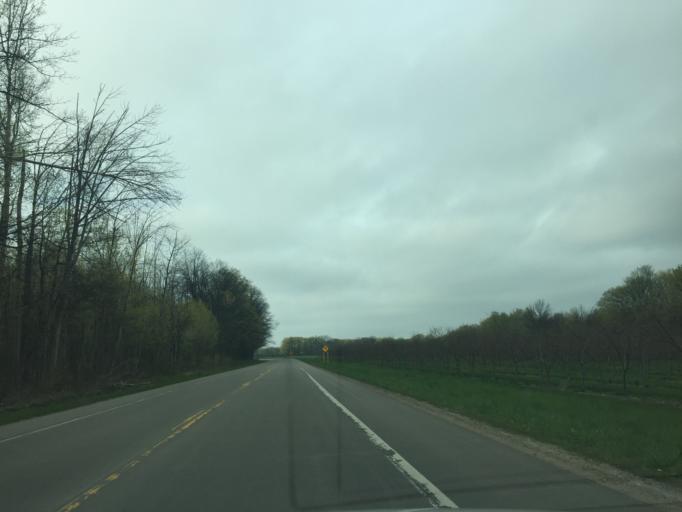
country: US
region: Michigan
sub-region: Leelanau County
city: Leland
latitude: 45.0672
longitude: -85.5872
